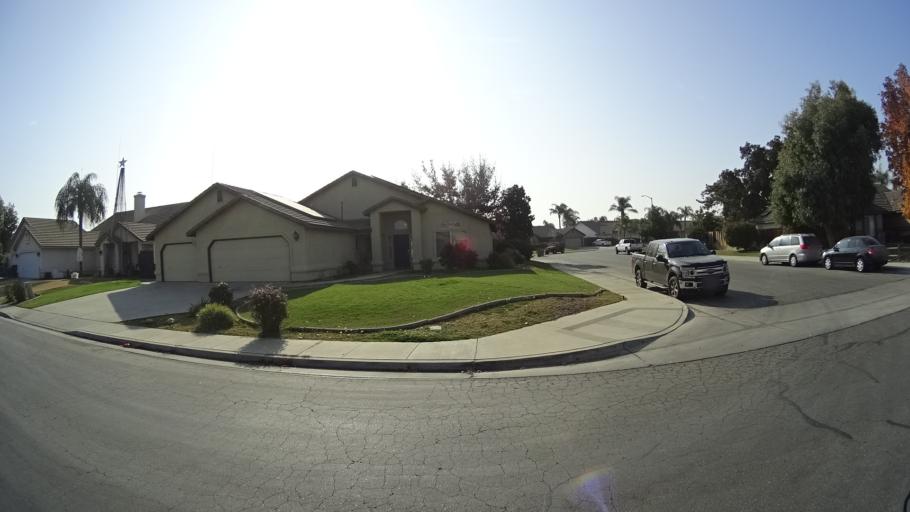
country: US
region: California
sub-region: Kern County
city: Greenacres
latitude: 35.4077
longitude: -119.1117
